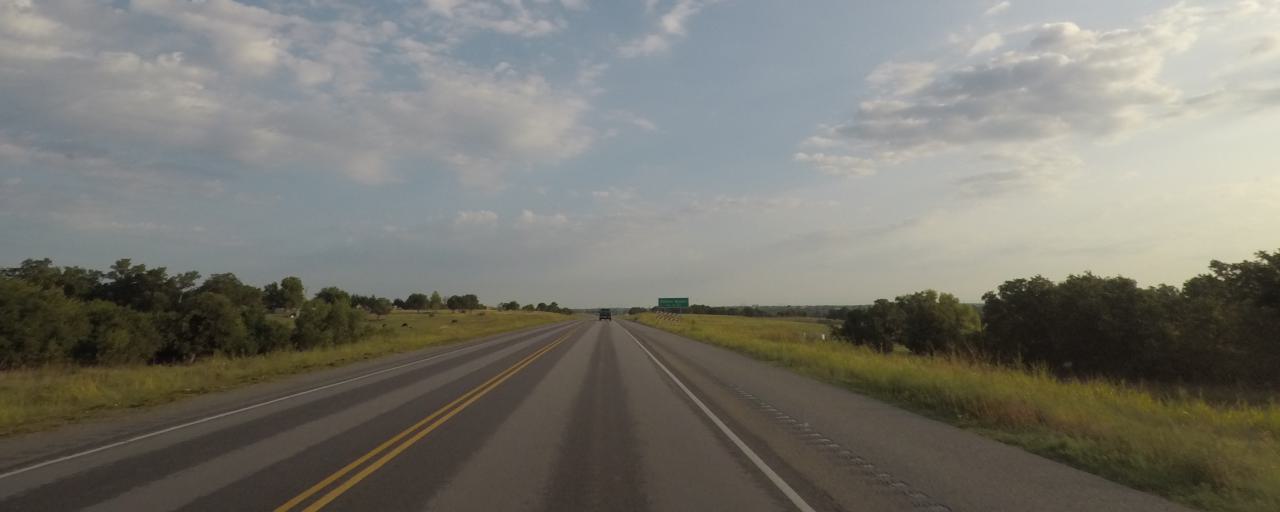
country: US
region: Oklahoma
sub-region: Stephens County
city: Meridian
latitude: 34.4517
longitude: -97.9741
